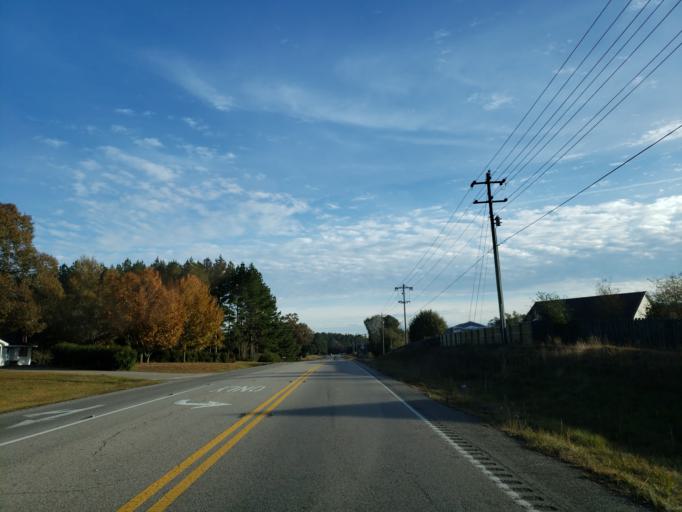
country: US
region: Mississippi
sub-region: Lamar County
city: West Hattiesburg
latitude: 31.2834
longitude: -89.4680
